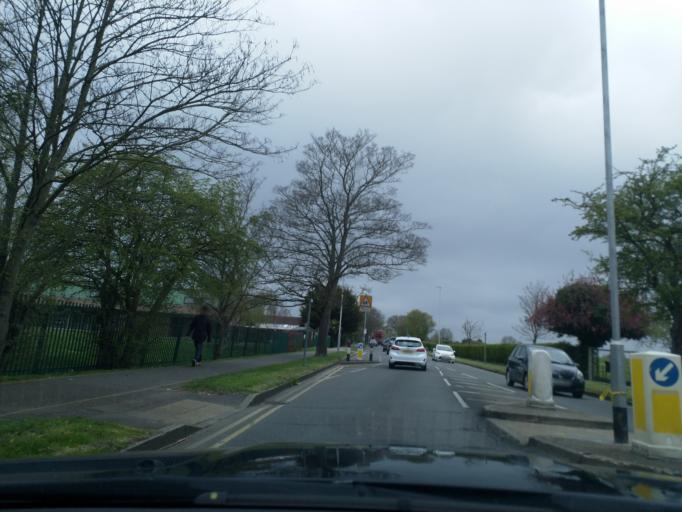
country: GB
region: England
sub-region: Greater London
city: Northolt
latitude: 51.5660
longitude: -0.3862
